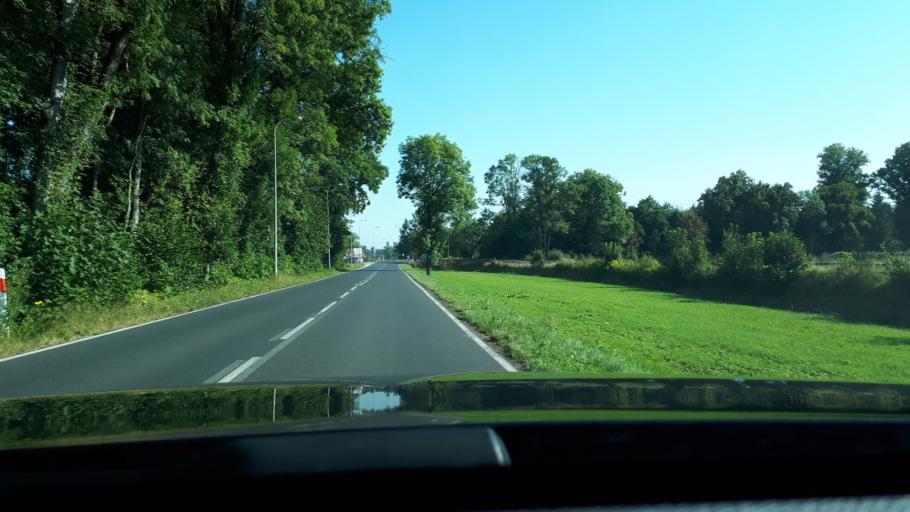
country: PL
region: Lower Silesian Voivodeship
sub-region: Powiat lubanski
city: Luban
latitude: 51.0742
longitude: 15.2941
